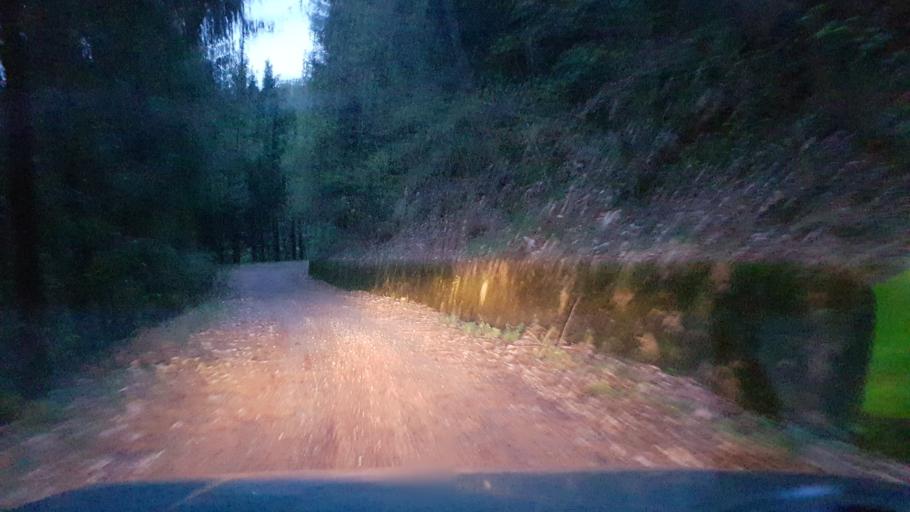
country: IT
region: Friuli Venezia Giulia
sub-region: Provincia di Udine
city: Taipana
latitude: 46.2266
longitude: 13.3537
